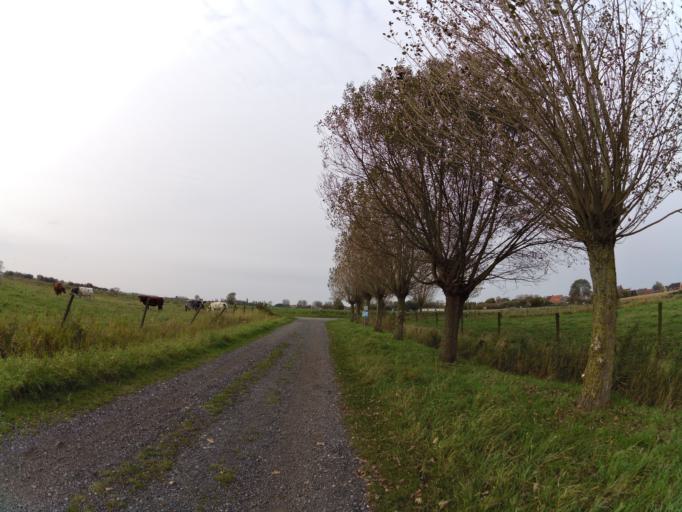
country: BE
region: Flanders
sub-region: Provincie West-Vlaanderen
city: Jabbeke
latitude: 51.2075
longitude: 3.0744
